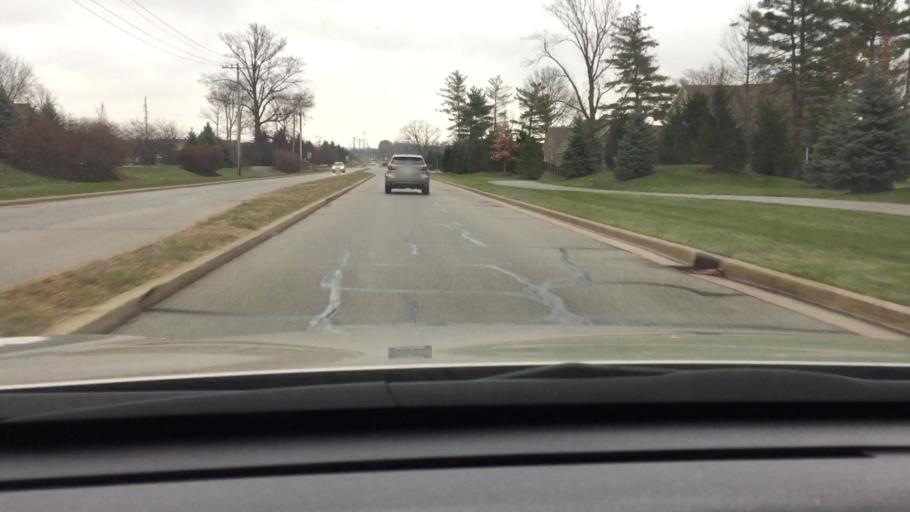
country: US
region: Indiana
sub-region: Hamilton County
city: Carmel
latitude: 40.0075
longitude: -86.0983
